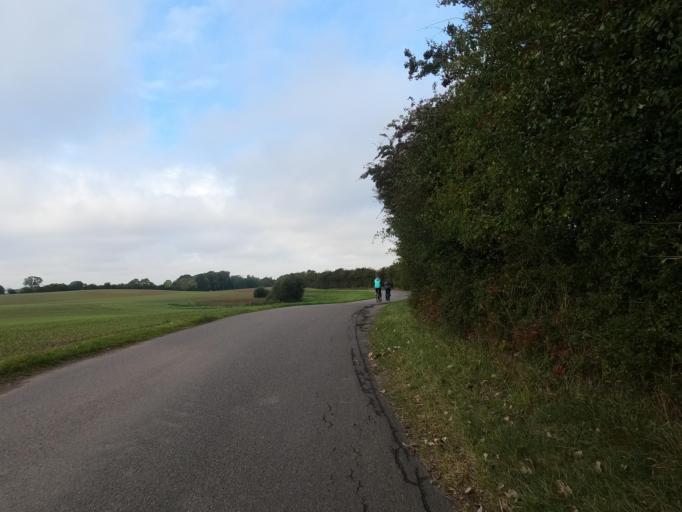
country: DE
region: Schleswig-Holstein
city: Neukirchen
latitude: 54.3096
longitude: 11.0496
